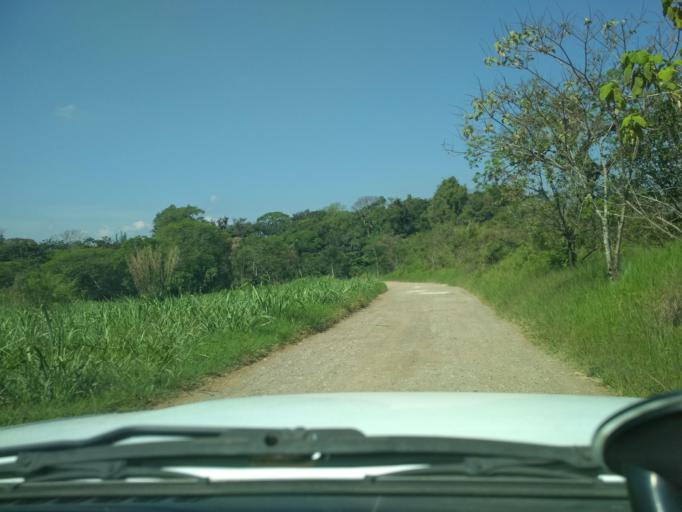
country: MX
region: Veracruz
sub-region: Fortin
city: Fraccionamiento los Alamos
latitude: 18.9216
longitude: -96.9801
